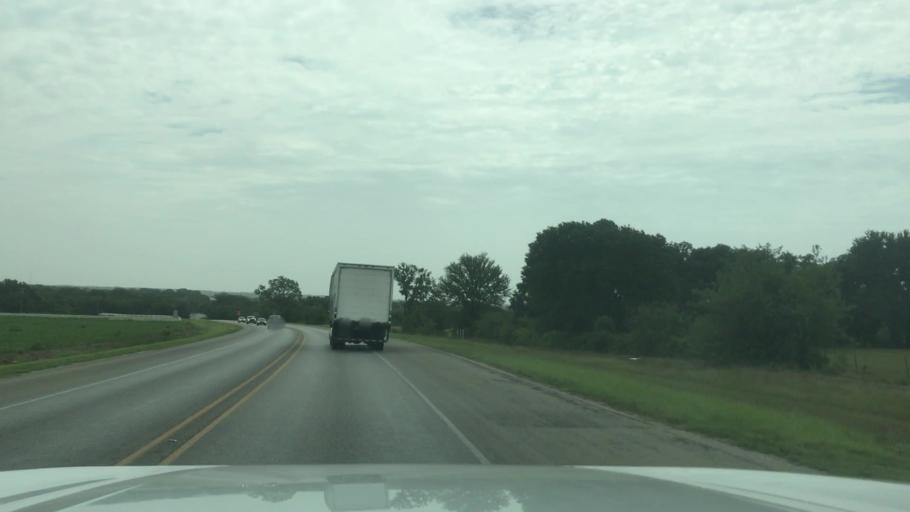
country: US
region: Texas
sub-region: Comanche County
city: De Leon
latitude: 32.1052
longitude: -98.4882
